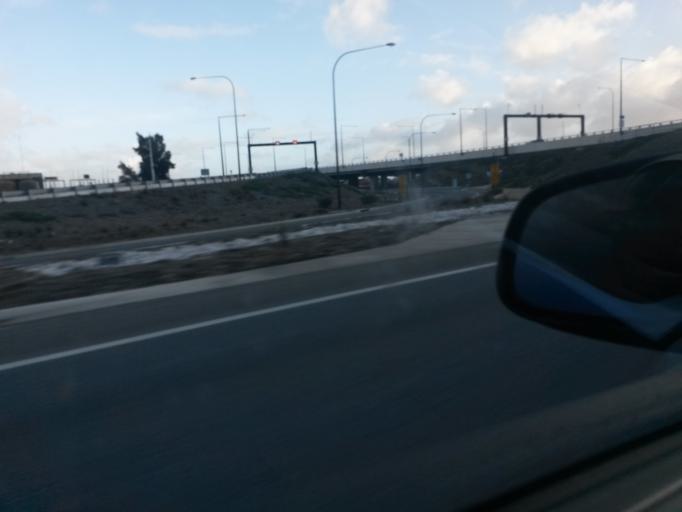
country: AU
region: South Australia
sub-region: Port Adelaide Enfield
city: Blair Athol
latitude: -34.8328
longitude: 138.5641
